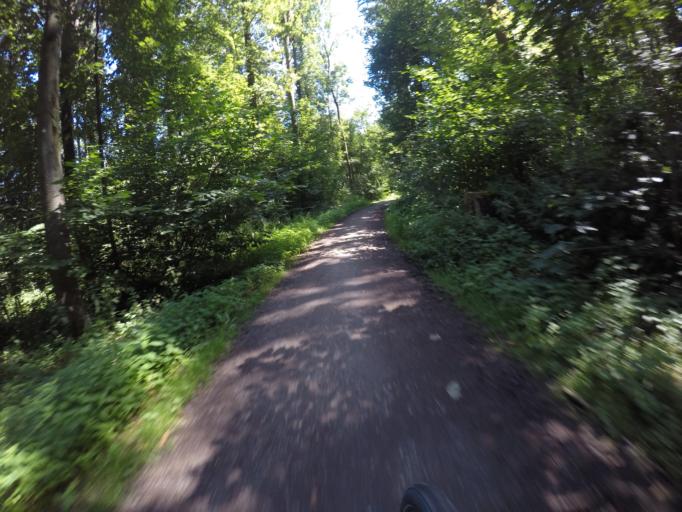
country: DE
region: Baden-Wuerttemberg
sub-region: Regierungsbezirk Stuttgart
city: Leinfelden-Echterdingen
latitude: 48.7157
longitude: 9.1690
